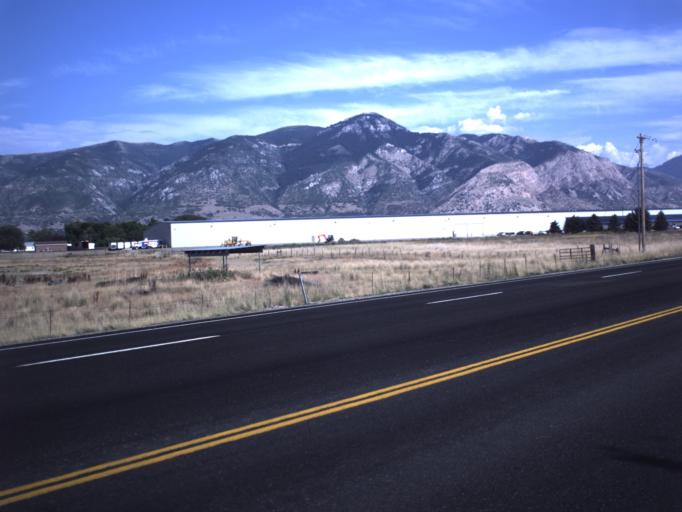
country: US
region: Utah
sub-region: Weber County
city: Pleasant View
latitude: 41.3110
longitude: -112.0092
